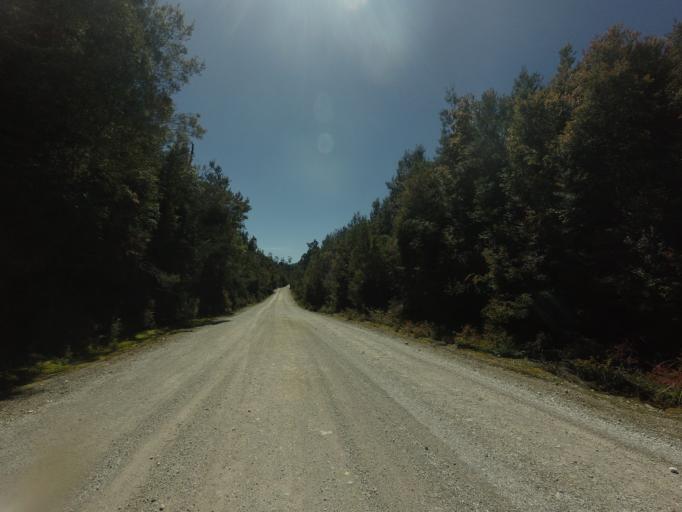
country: AU
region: Tasmania
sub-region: Huon Valley
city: Geeveston
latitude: -42.8321
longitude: 146.3851
